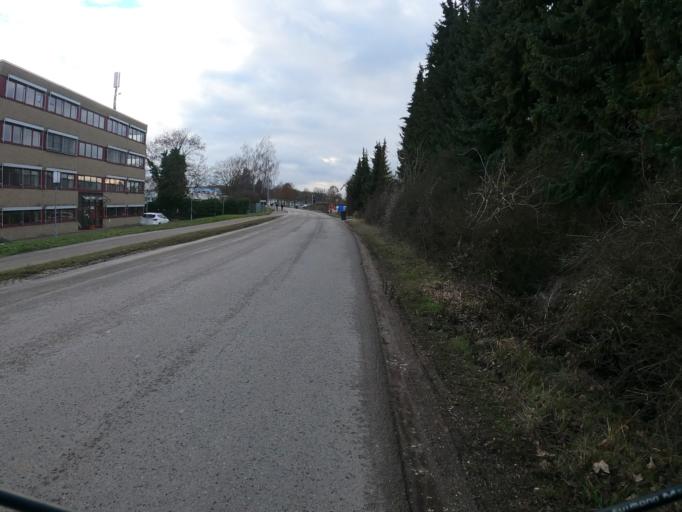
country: DE
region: Bavaria
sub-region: Swabia
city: Nersingen
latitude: 48.4525
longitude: 10.0997
